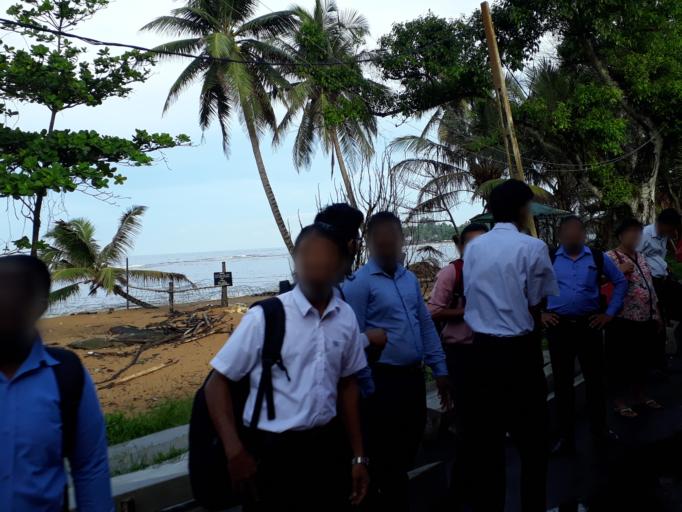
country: LK
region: Western
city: Kalutara
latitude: 6.5833
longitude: 79.9590
